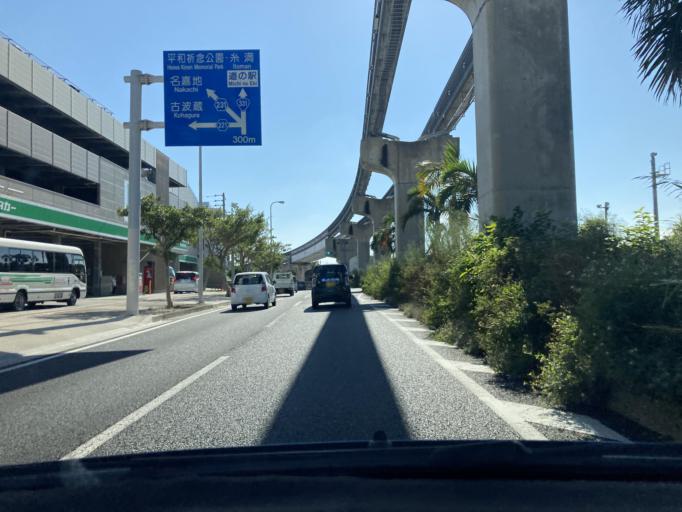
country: JP
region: Okinawa
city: Tomigusuku
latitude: 26.1966
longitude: 127.6598
